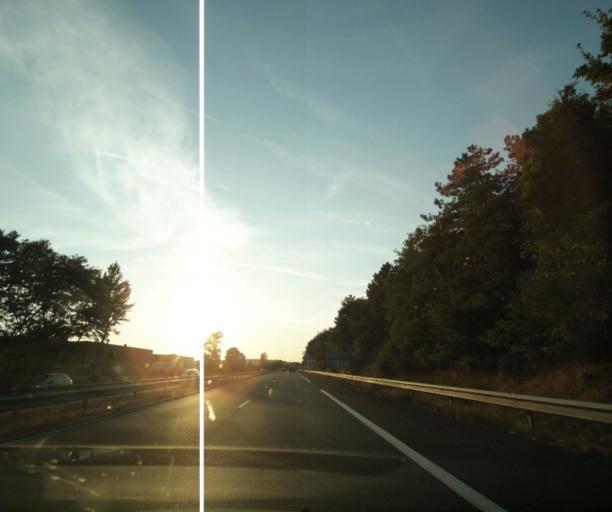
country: FR
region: Aquitaine
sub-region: Departement du Lot-et-Garonne
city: Estillac
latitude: 44.1637
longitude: 0.5948
